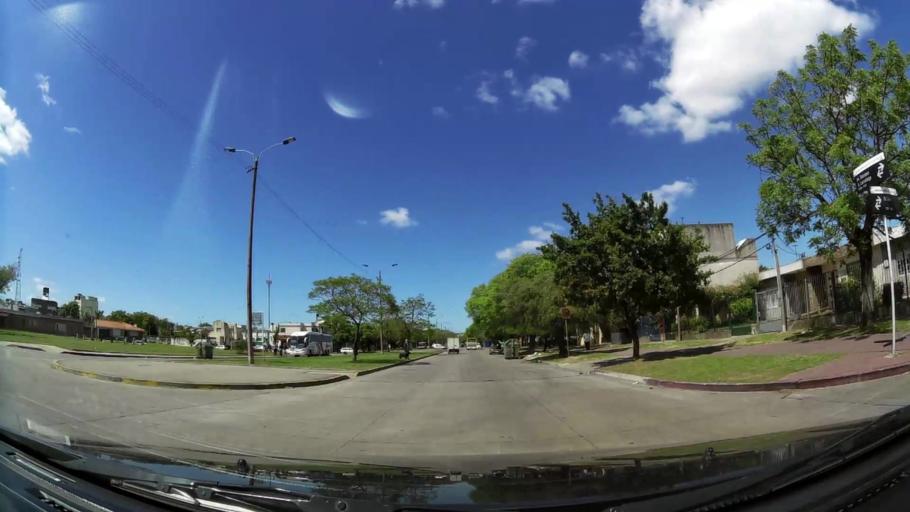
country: UY
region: Montevideo
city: Montevideo
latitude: -34.8587
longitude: -56.1508
